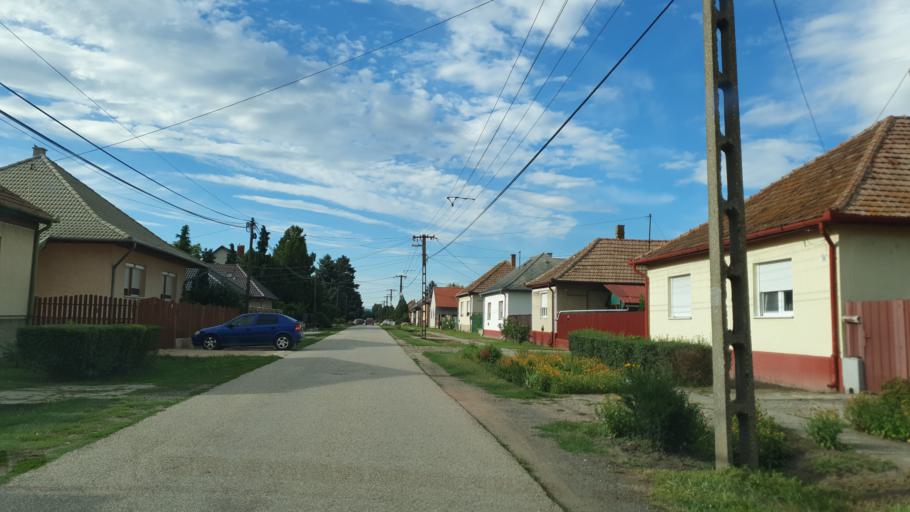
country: HU
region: Heves
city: Zagyvaszanto
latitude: 47.7580
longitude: 19.6792
